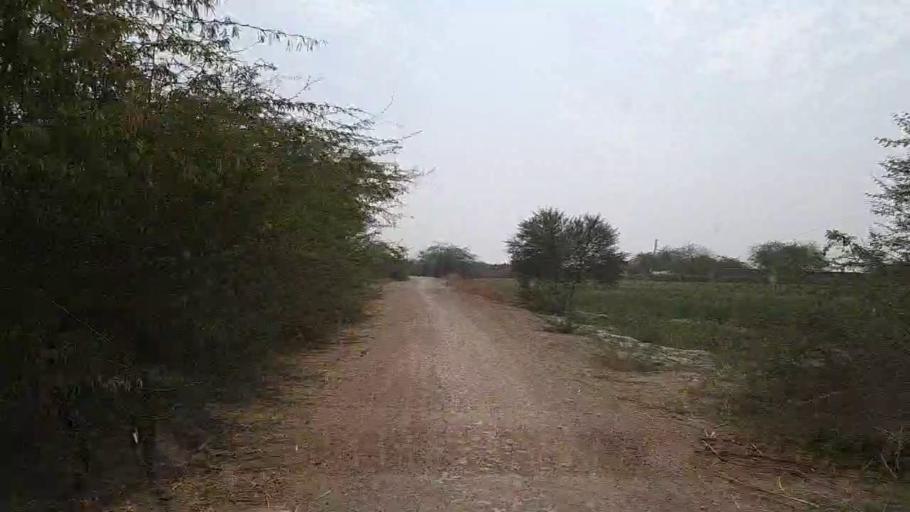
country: PK
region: Sindh
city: Mirwah Gorchani
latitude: 25.3437
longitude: 69.0786
